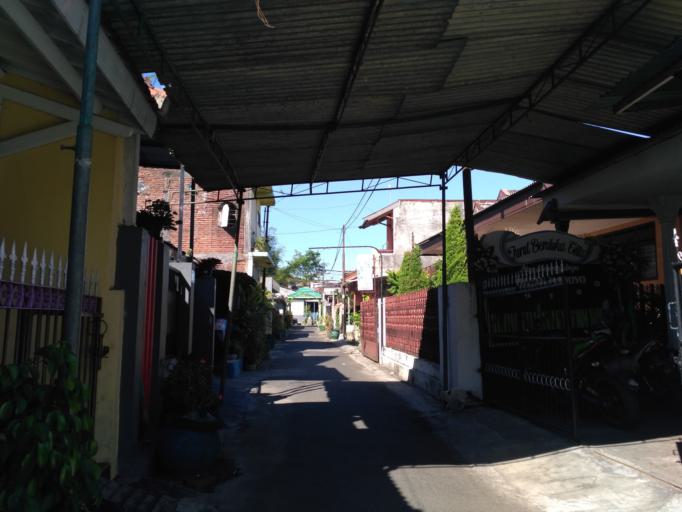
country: ID
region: East Java
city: Singosari
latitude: -7.9281
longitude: 112.6518
